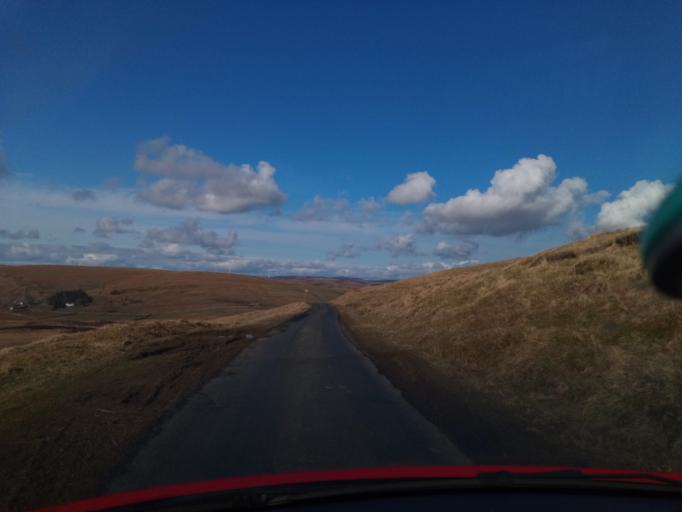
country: GB
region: Scotland
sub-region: The Scottish Borders
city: Hawick
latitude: 55.4455
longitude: -2.8869
